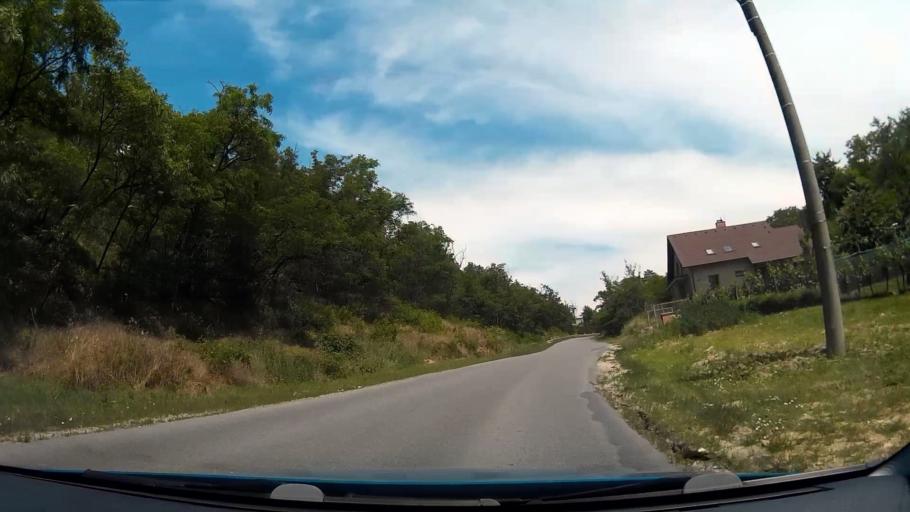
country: CZ
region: South Moravian
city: Dolni Kounice
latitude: 49.0526
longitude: 16.5024
